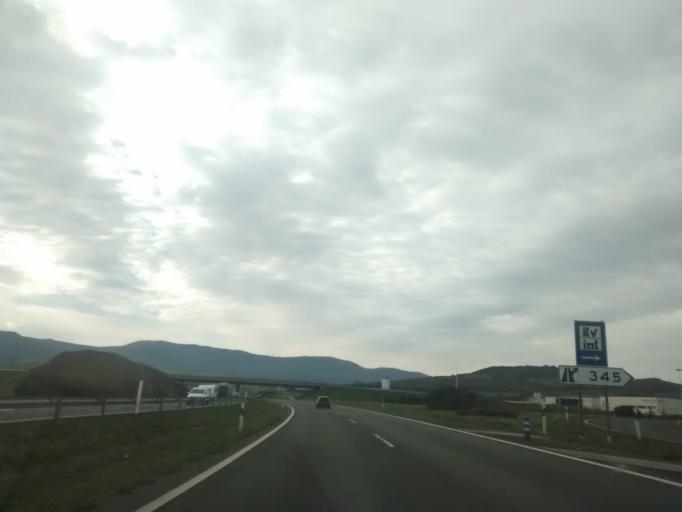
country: ES
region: Basque Country
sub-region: Provincia de Alava
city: Gasteiz / Vitoria
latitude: 42.8453
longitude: -2.7509
